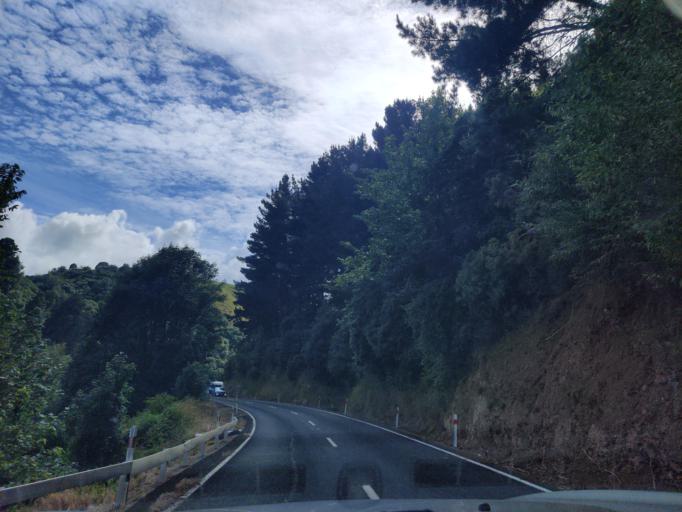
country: NZ
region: Waikato
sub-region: Otorohanga District
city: Otorohanga
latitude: -38.0974
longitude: 175.1240
